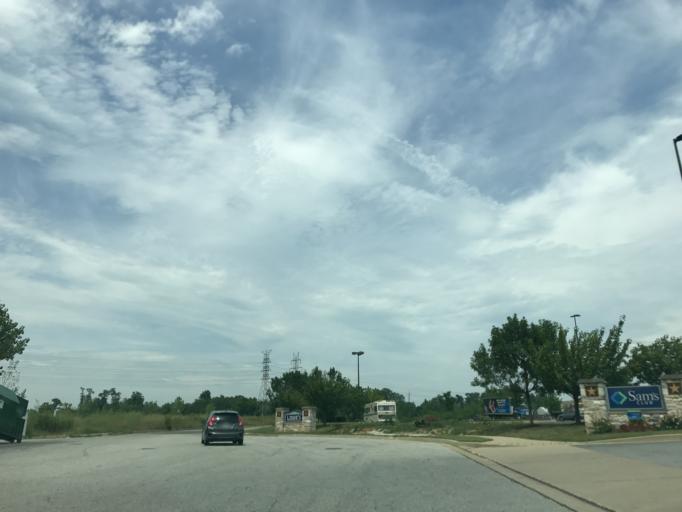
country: US
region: Maryland
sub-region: Baltimore County
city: Cockeysville
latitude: 39.4580
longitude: -76.6402
